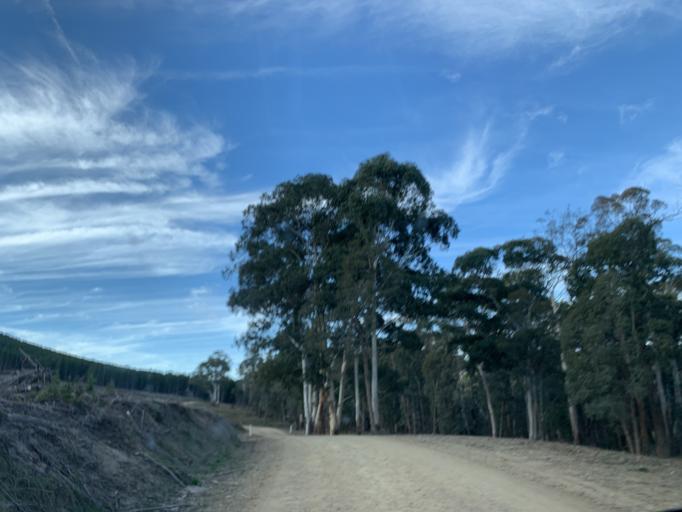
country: AU
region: Victoria
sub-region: Mansfield
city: Mansfield
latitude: -36.9282
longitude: 146.0951
